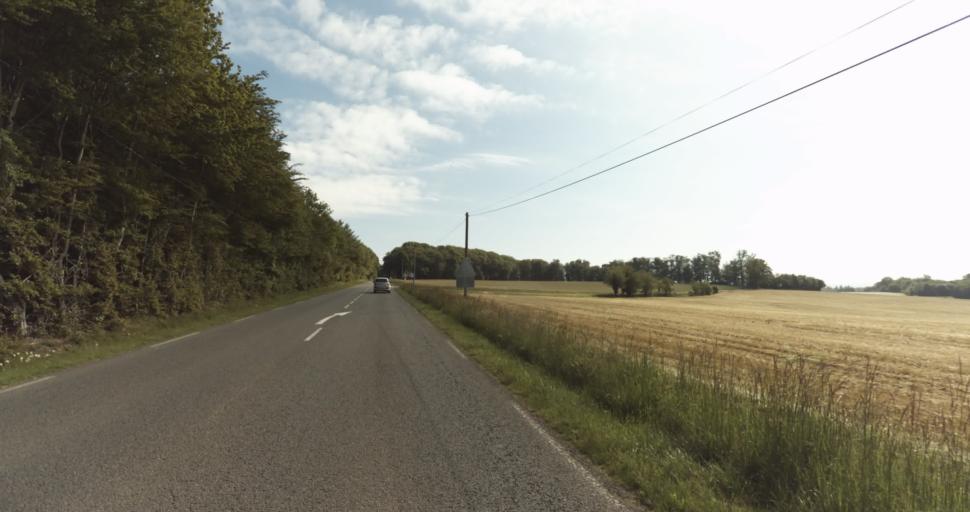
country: FR
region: Limousin
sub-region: Departement de la Haute-Vienne
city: Solignac
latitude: 45.7201
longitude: 1.2540
